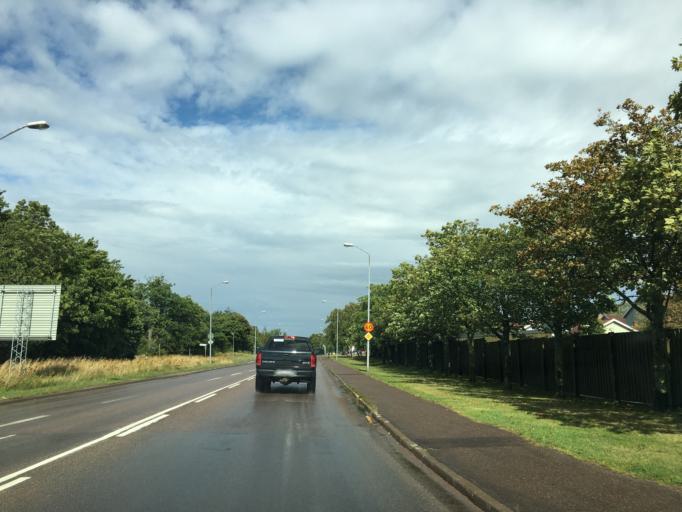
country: SE
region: Kalmar
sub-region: Kalmar Kommun
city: Kalmar
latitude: 56.6954
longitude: 16.3326
